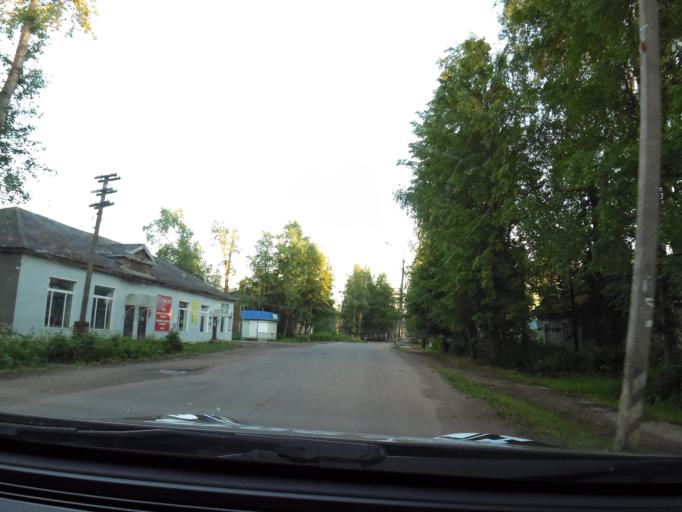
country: RU
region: Leningrad
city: Voznesen'ye
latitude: 61.0112
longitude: 35.4827
